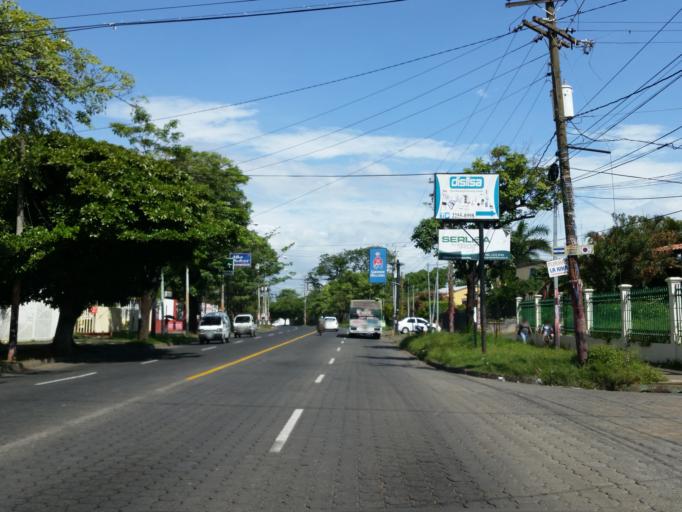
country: NI
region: Managua
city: Managua
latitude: 12.1356
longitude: -86.2852
